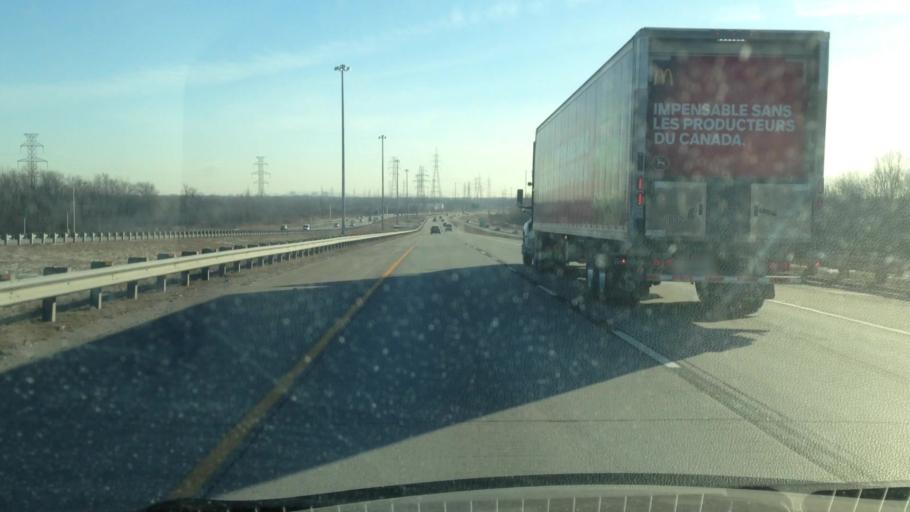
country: CA
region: Quebec
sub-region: Laurentides
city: Boisbriand
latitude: 45.5985
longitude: -73.8620
